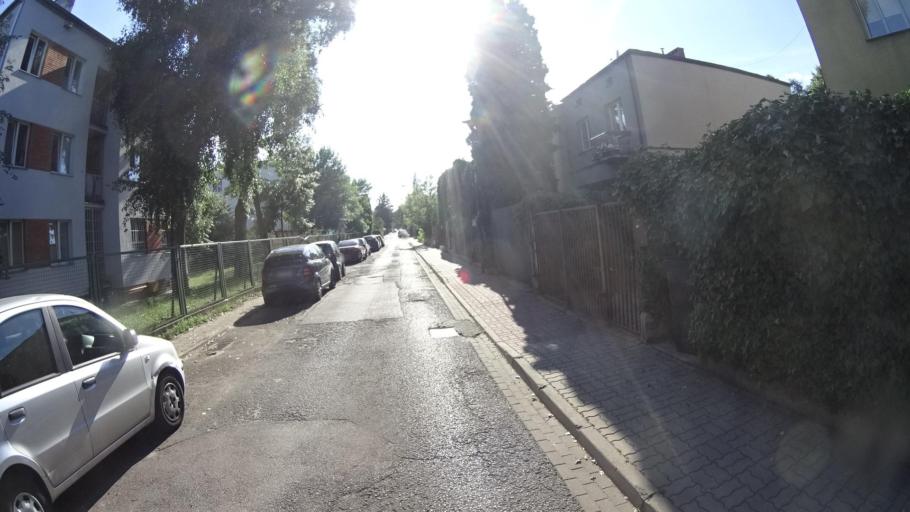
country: PL
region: Masovian Voivodeship
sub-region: Warszawa
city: Wola
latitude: 52.2479
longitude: 20.9487
